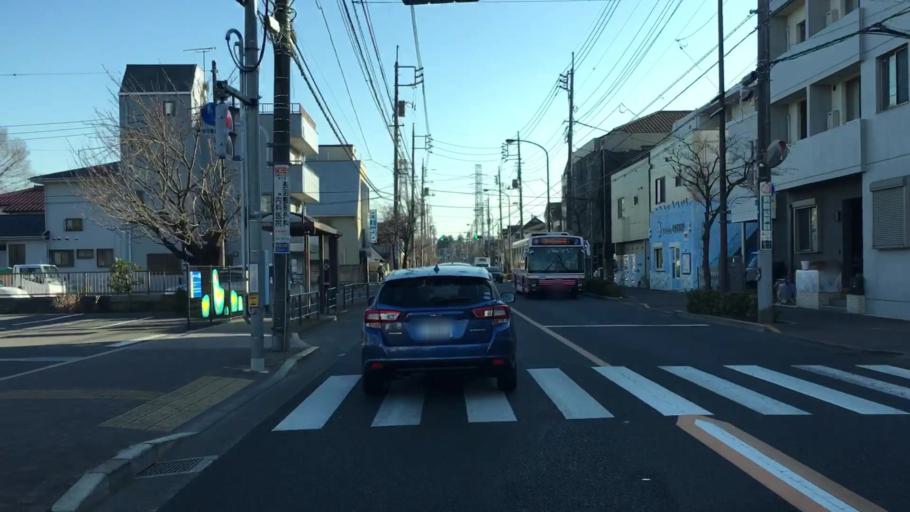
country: JP
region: Tokyo
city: Kamirenjaku
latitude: 35.6928
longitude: 139.5377
